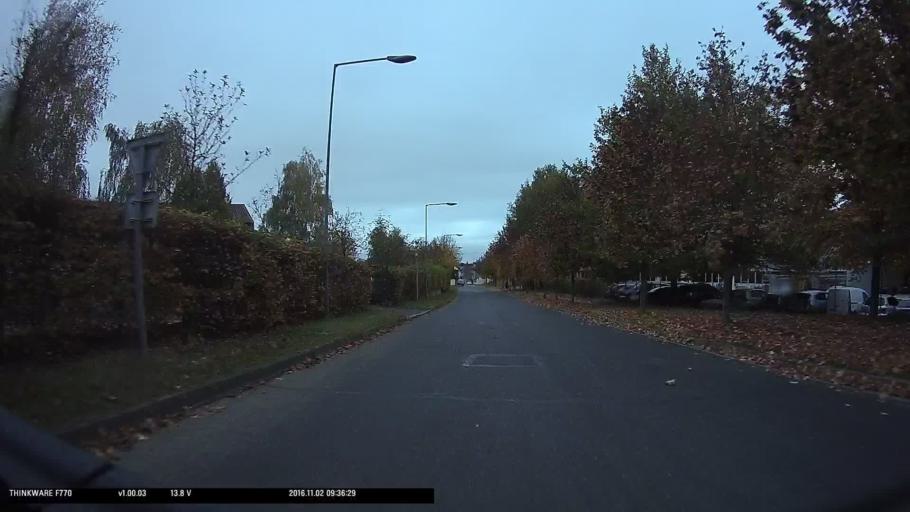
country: FR
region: Ile-de-France
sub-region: Departement du Val-d'Oise
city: Vaureal
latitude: 49.0556
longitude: 2.0252
